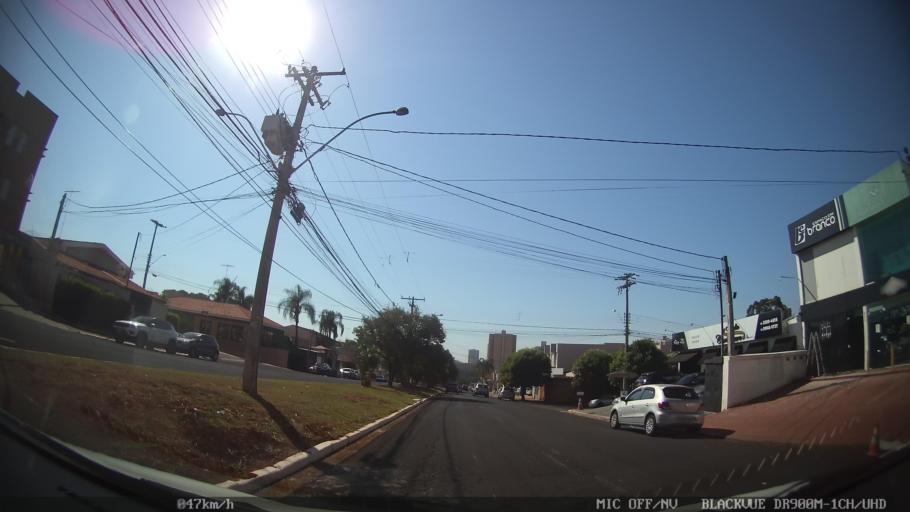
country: BR
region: Sao Paulo
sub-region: Ribeirao Preto
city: Ribeirao Preto
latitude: -21.2014
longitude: -47.8047
